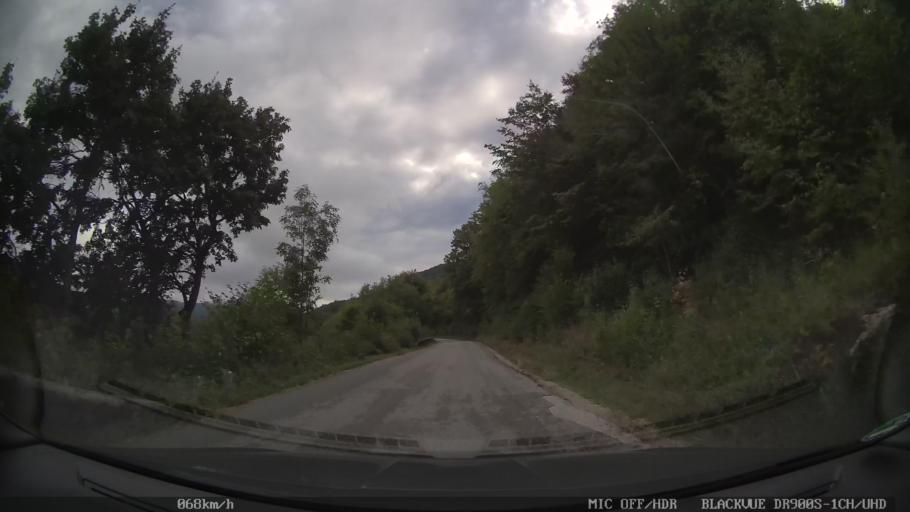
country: HR
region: Licko-Senjska
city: Jezerce
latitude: 44.9285
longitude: 15.6177
